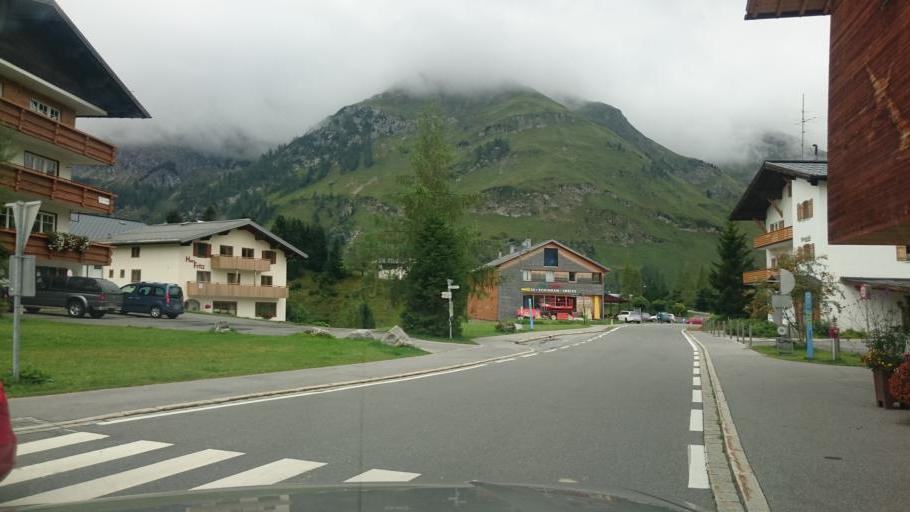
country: AT
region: Vorarlberg
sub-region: Politischer Bezirk Bregenz
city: Warth
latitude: 47.2579
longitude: 10.1833
